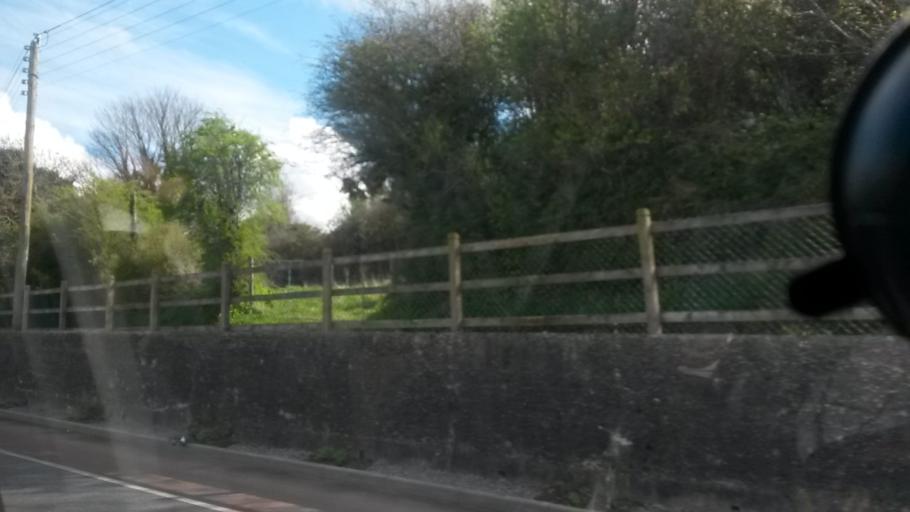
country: IE
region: Ulster
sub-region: An Cabhan
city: Cavan
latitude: 53.9997
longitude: -7.3549
